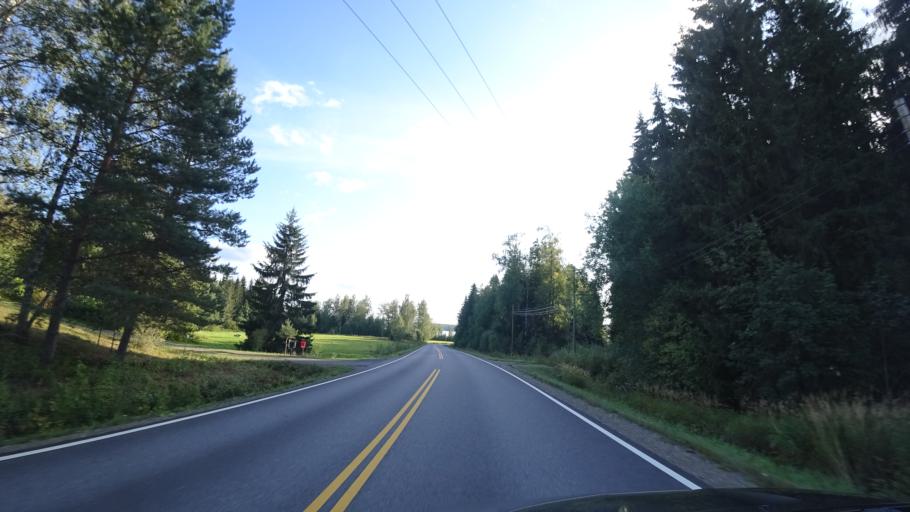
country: FI
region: Paijanne Tavastia
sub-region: Lahti
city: Haemeenkoski
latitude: 61.0845
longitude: 25.1398
